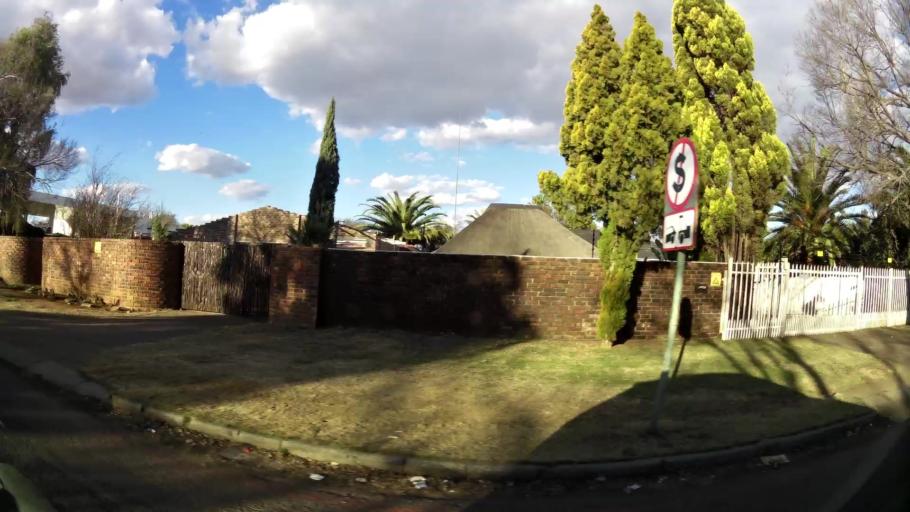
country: ZA
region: North-West
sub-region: Dr Kenneth Kaunda District Municipality
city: Potchefstroom
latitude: -26.7277
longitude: 27.0844
